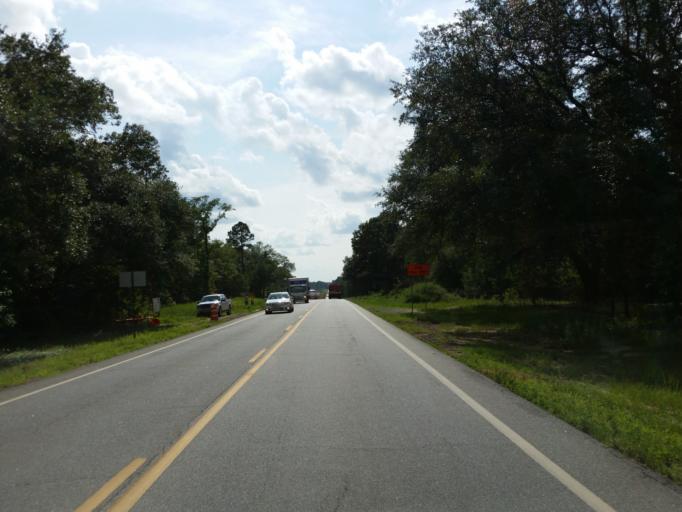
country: US
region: Georgia
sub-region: Lee County
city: Leesburg
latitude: 31.7248
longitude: -84.0100
